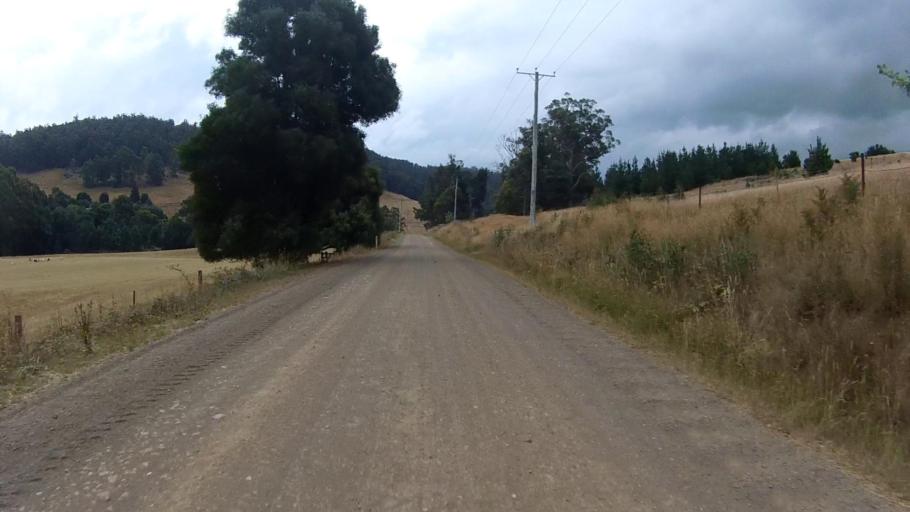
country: AU
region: Tasmania
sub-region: Huon Valley
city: Huonville
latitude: -42.9731
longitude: 147.0542
